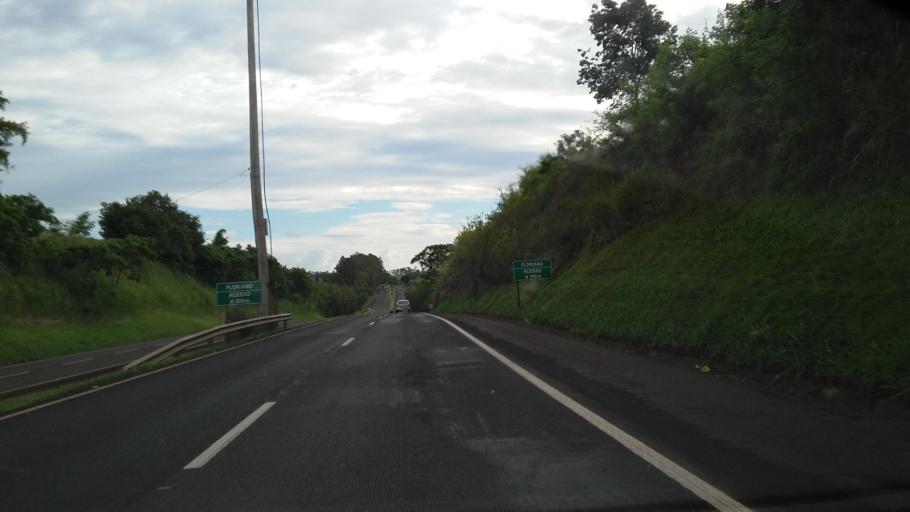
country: BR
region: Parana
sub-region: Paicandu
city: Paicandu
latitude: -23.5167
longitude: -52.0276
